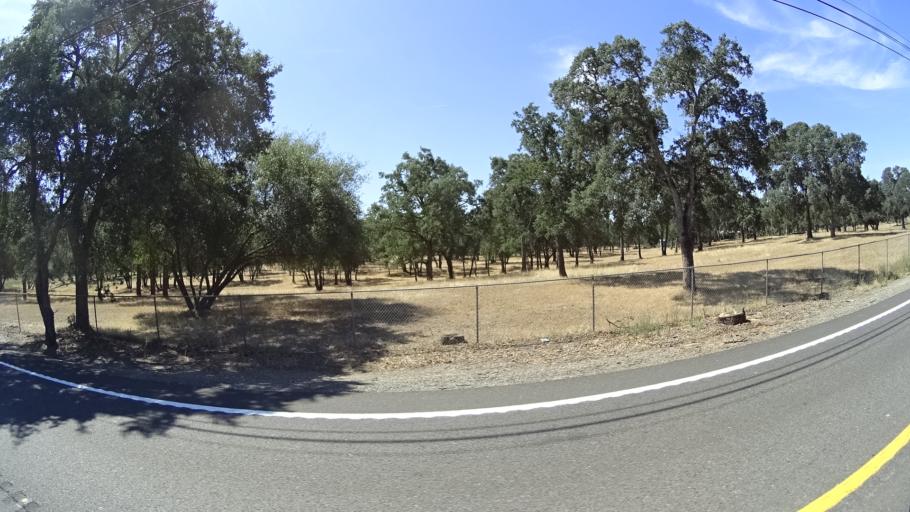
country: US
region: California
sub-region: Calaveras County
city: Rancho Calaveras
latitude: 38.1815
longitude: -120.9055
